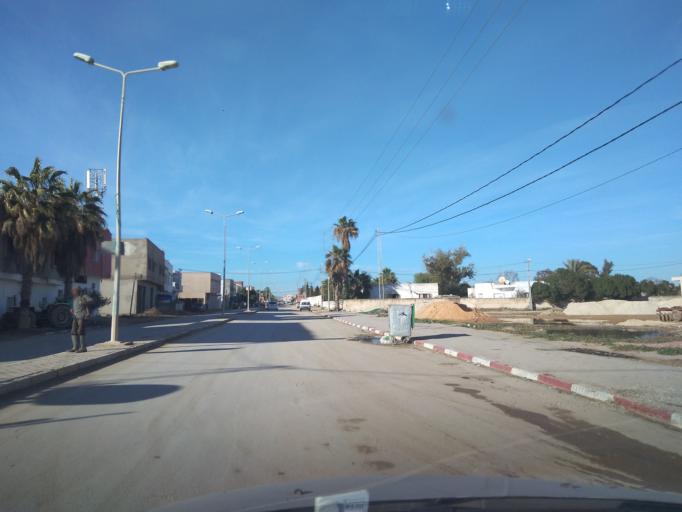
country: TN
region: Ariana
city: Qal'at al Andalus
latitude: 37.0557
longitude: 10.1209
